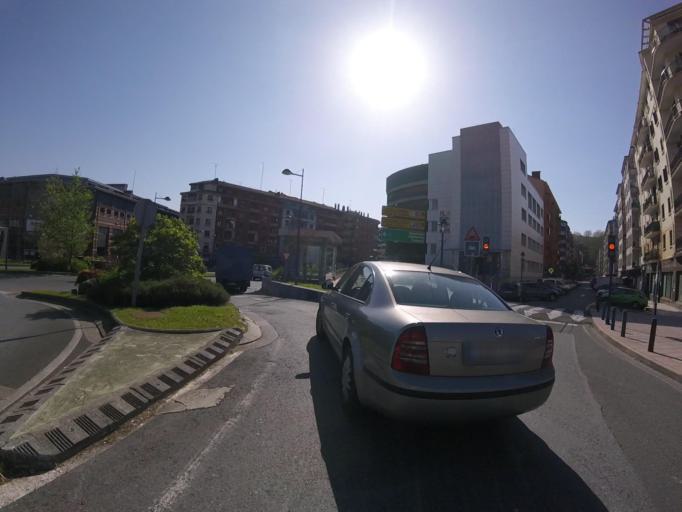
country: ES
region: Basque Country
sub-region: Provincia de Guipuzcoa
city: Errenteria
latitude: 43.3153
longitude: -1.9004
